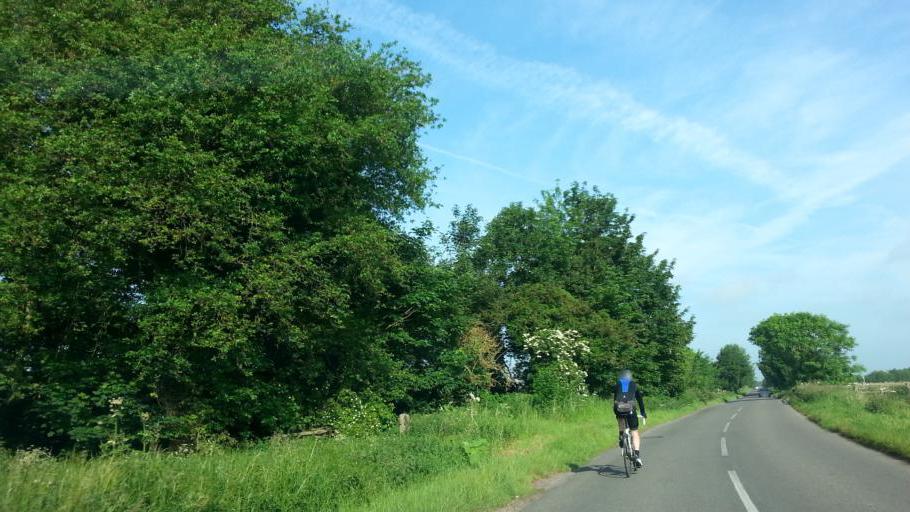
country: GB
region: England
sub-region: Nottinghamshire
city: Farndon
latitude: 53.0492
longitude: -0.8345
